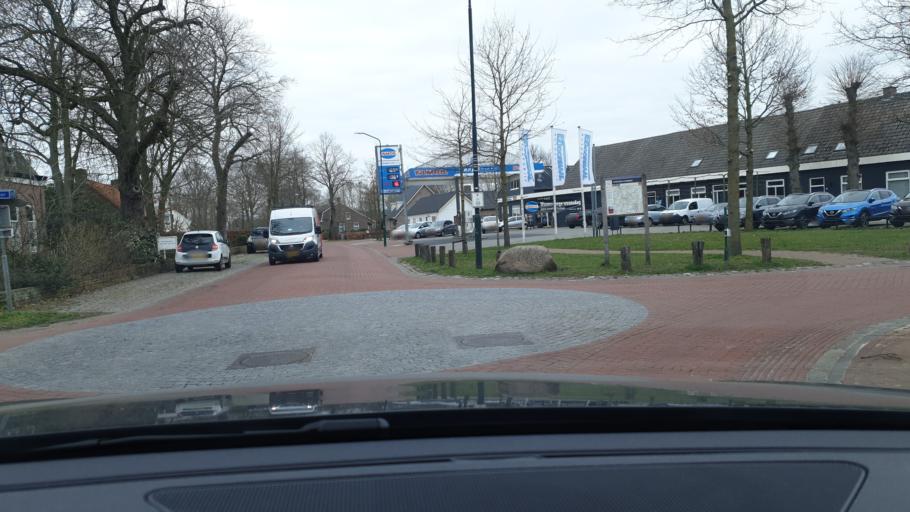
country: NL
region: North Brabant
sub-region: Gemeente Oirschot
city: Oostelbeers
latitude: 51.4238
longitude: 5.2850
